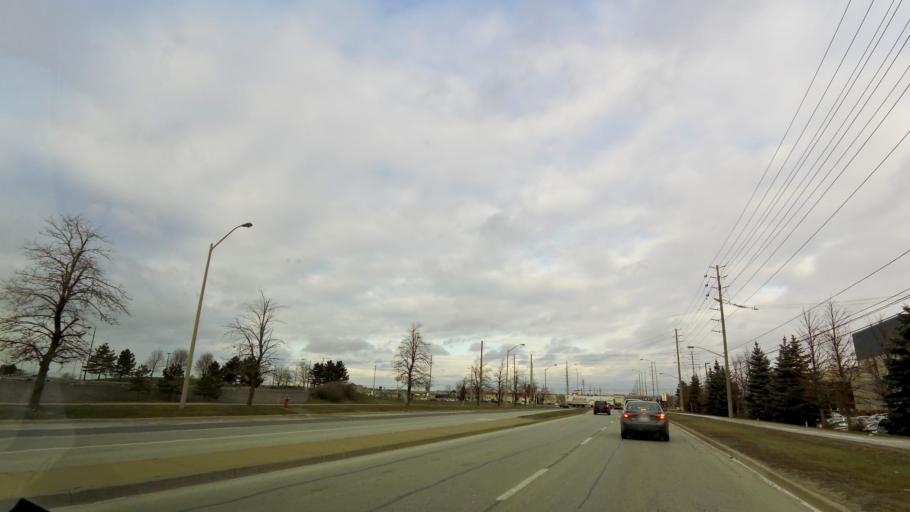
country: CA
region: Ontario
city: Brampton
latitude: 43.7520
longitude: -79.7103
